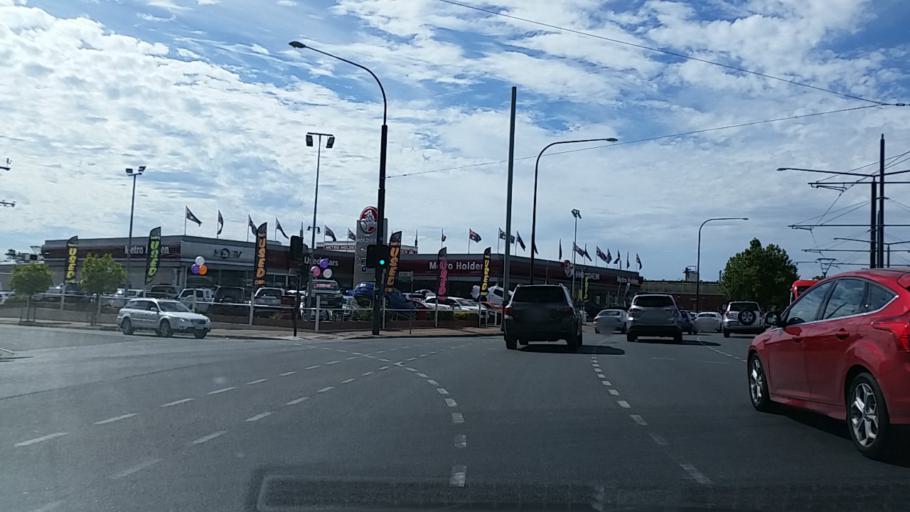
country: AU
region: South Australia
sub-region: City of West Torrens
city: Thebarton
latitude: -34.9188
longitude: 138.5788
